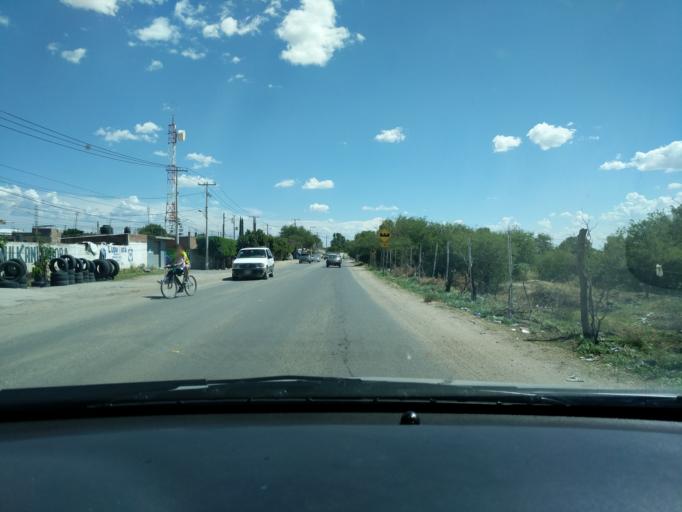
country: MX
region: Guanajuato
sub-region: Leon
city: Ladrilleras del Refugio
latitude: 21.0743
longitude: -101.5477
